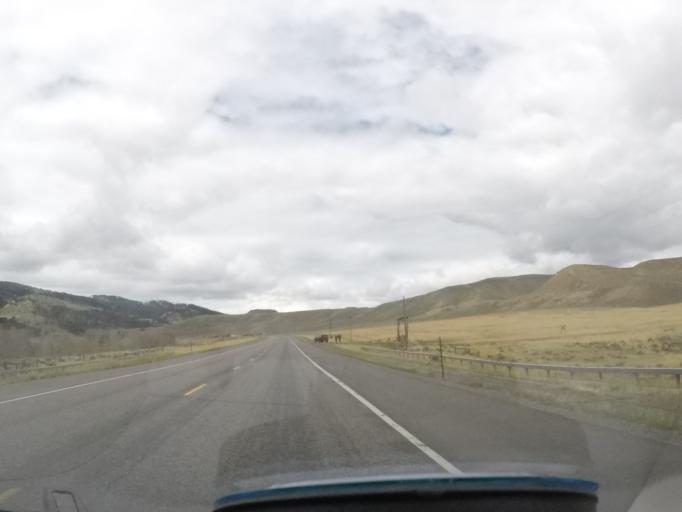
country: US
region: Wyoming
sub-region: Sublette County
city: Pinedale
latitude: 43.5770
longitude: -109.7380
